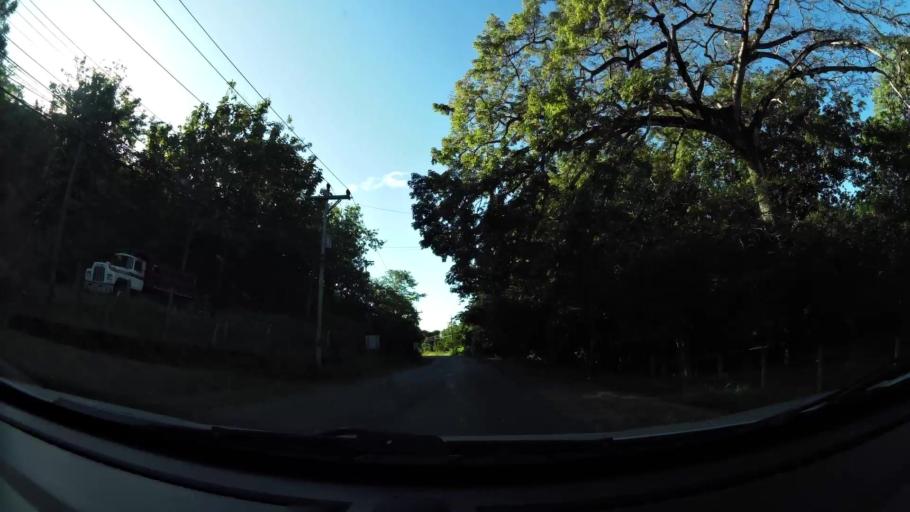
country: CR
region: Guanacaste
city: Sardinal
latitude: 10.5215
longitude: -85.6497
